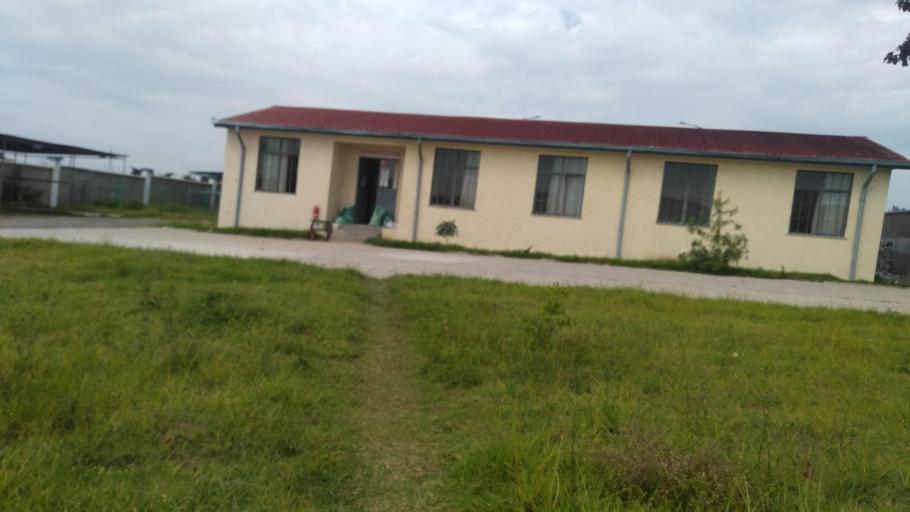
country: ET
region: Oromiya
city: Shashemene
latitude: 7.1691
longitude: 38.5433
